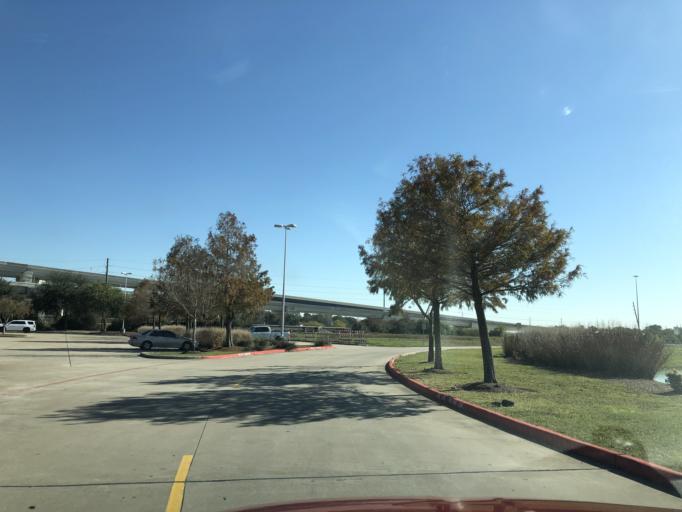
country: US
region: Texas
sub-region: Brazoria County
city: Brookside Village
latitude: 29.5943
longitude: -95.3887
